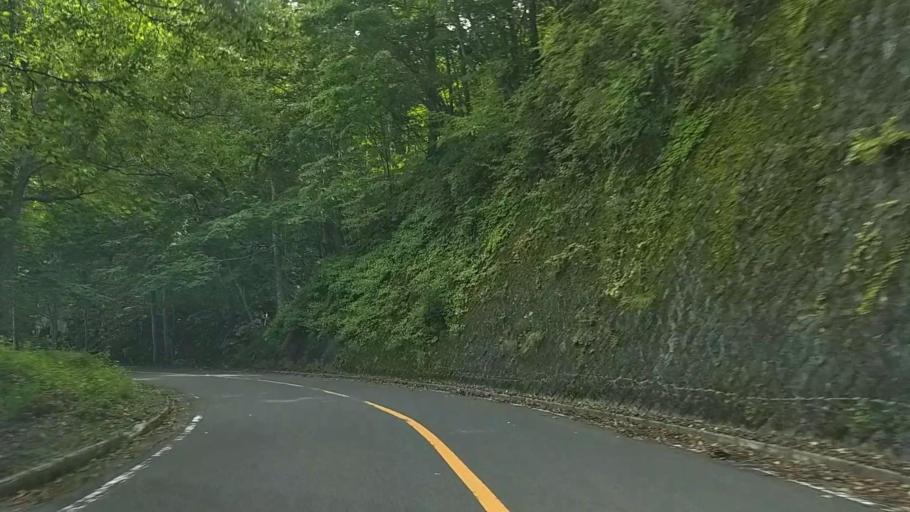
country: JP
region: Tochigi
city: Nikko
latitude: 36.7227
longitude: 139.4880
